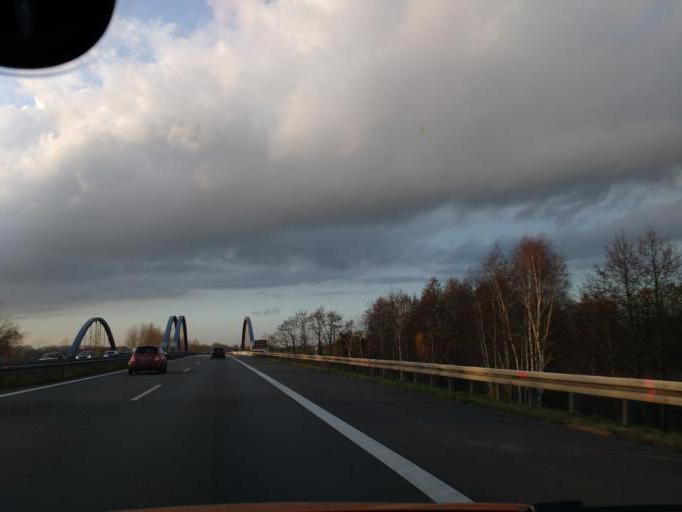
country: DE
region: Mecklenburg-Vorpommern
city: Neustadt-Glewe
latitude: 53.3933
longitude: 11.5972
